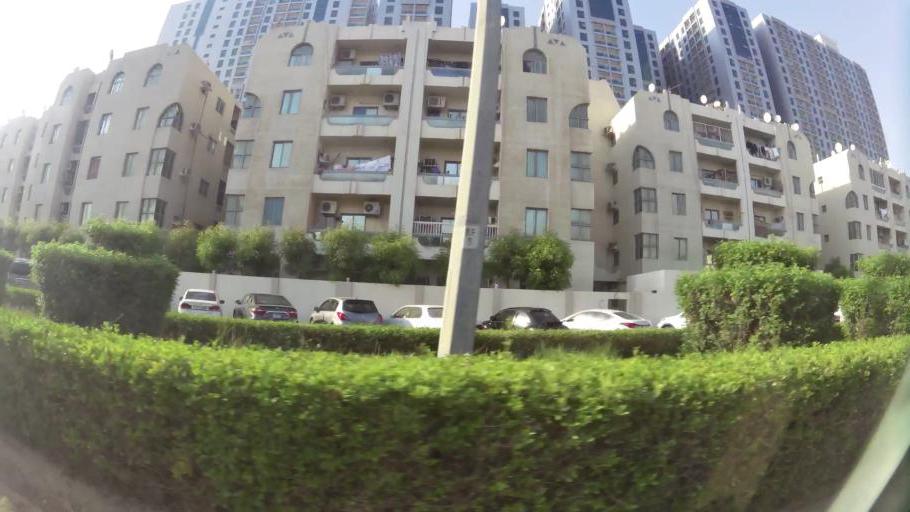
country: AE
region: Ajman
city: Ajman
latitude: 25.3897
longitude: 55.4409
